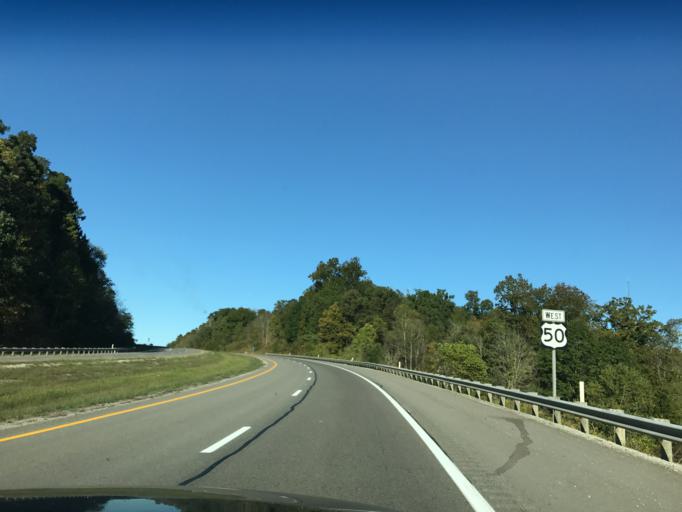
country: US
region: Ohio
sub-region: Washington County
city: Reno
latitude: 39.2424
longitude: -81.4102
